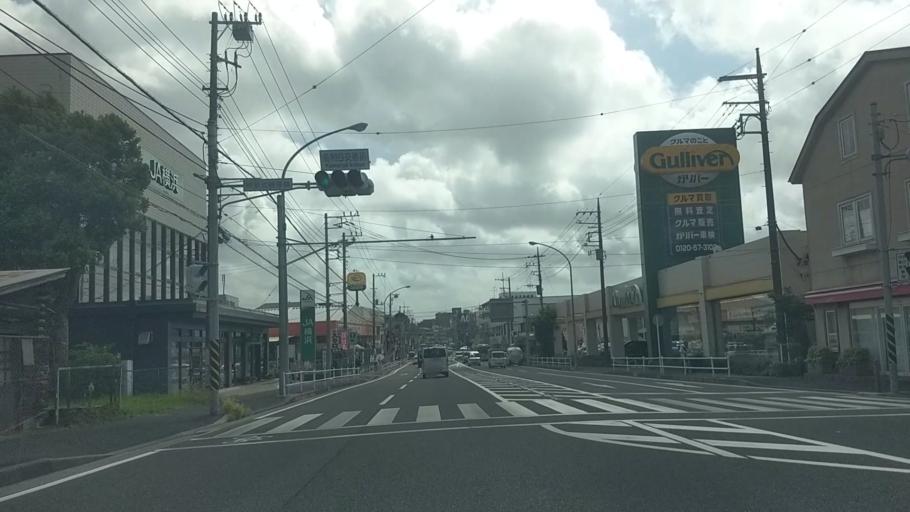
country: JP
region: Kanagawa
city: Zushi
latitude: 35.3448
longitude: 139.6112
